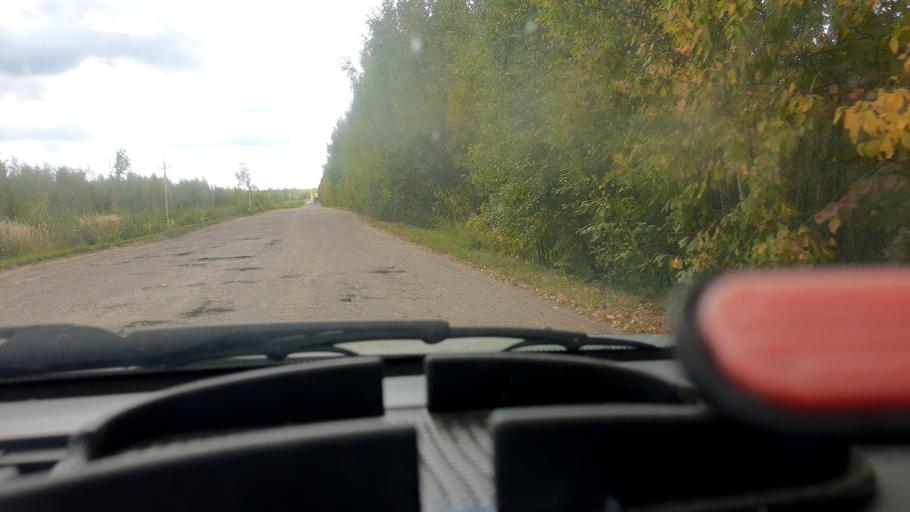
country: RU
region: Mariy-El
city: Kilemary
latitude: 56.8904
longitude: 46.7565
